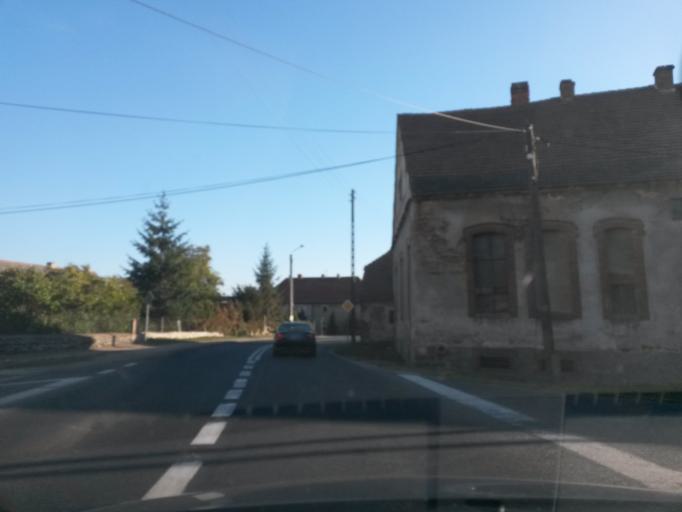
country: PL
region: Lower Silesian Voivodeship
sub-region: Powiat sredzki
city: Udanin
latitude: 51.0182
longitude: 16.4010
